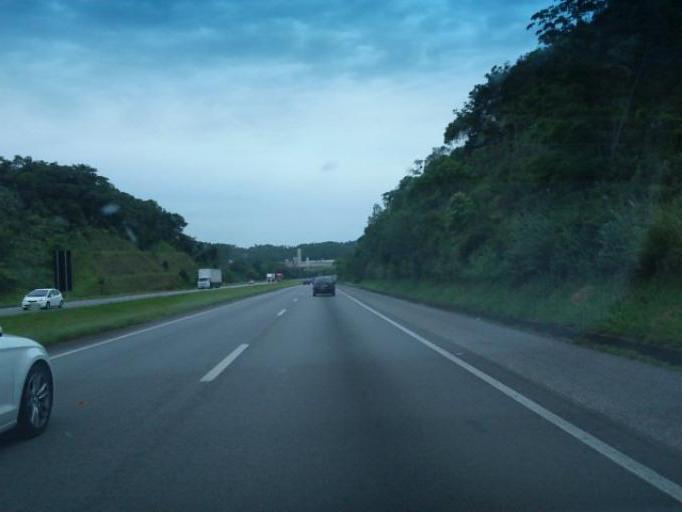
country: BR
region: Sao Paulo
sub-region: Registro
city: Registro
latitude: -24.5574
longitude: -47.8662
